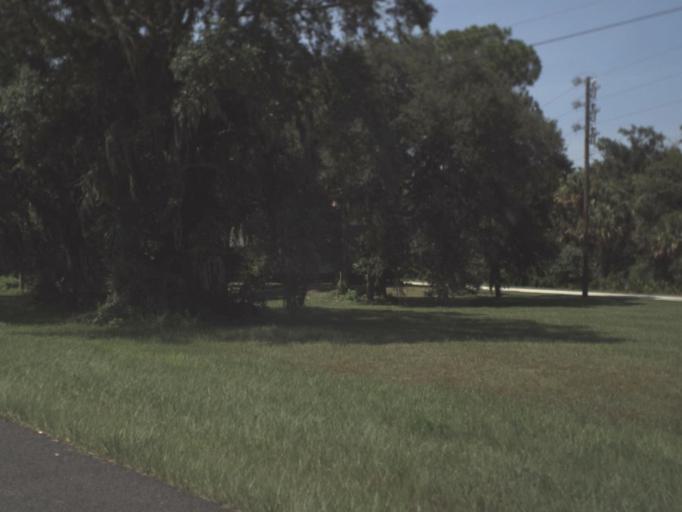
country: US
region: Florida
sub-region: Levy County
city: Inglis
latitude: 28.9743
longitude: -82.6376
